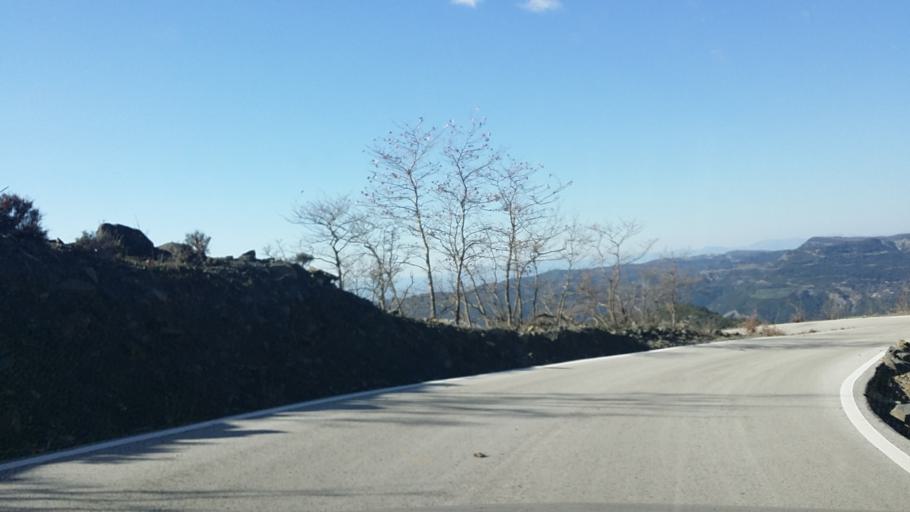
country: GR
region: West Greece
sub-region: Nomos Aitolias kai Akarnanias
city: Krikellos
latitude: 38.9772
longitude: 21.2731
